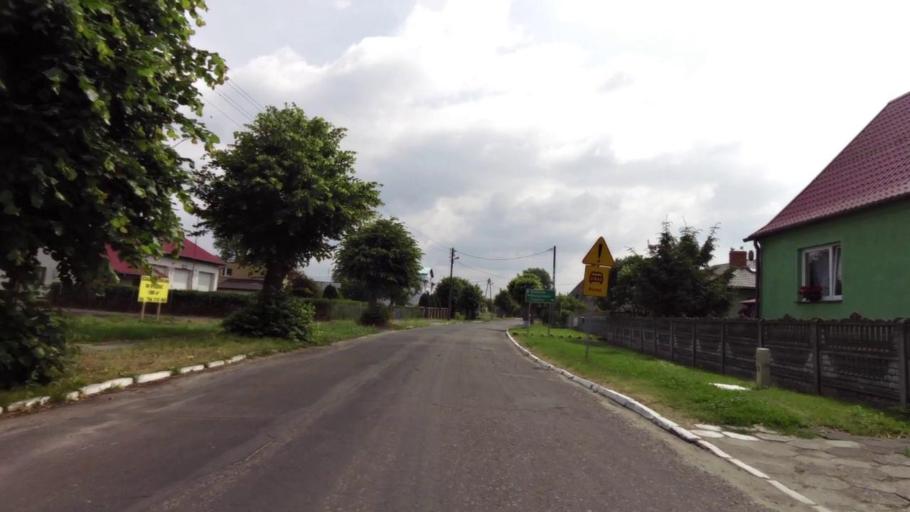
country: PL
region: West Pomeranian Voivodeship
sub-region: Powiat goleniowski
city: Goleniow
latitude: 53.5035
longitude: 14.7077
